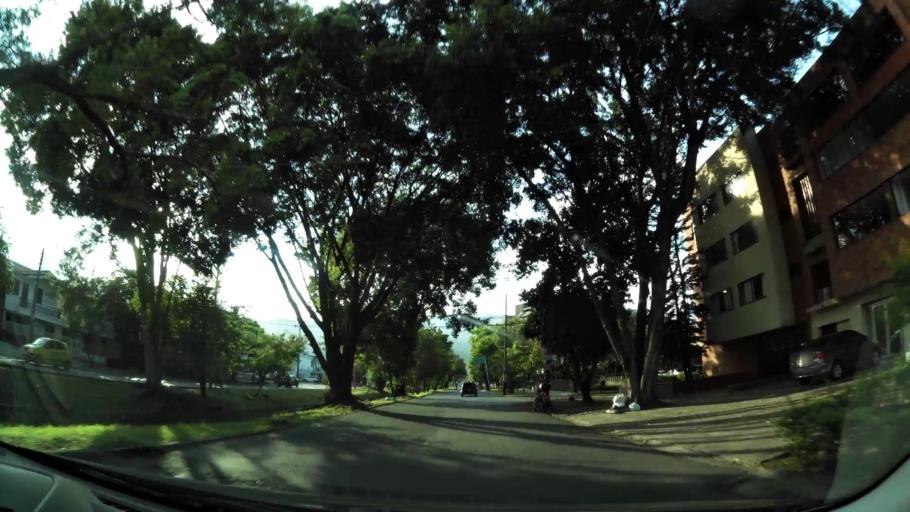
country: CO
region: Valle del Cauca
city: Cali
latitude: 3.4847
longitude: -76.5149
